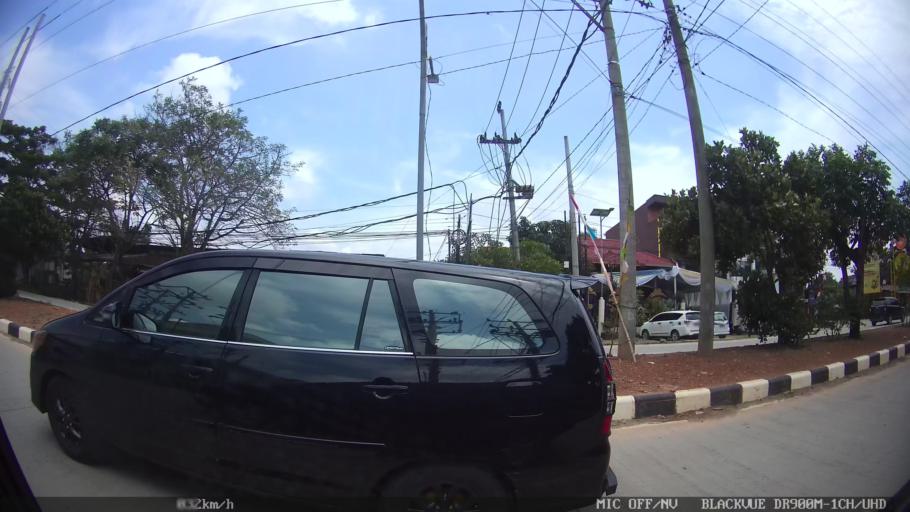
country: ID
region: Lampung
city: Kedaton
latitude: -5.3622
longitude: 105.3035
